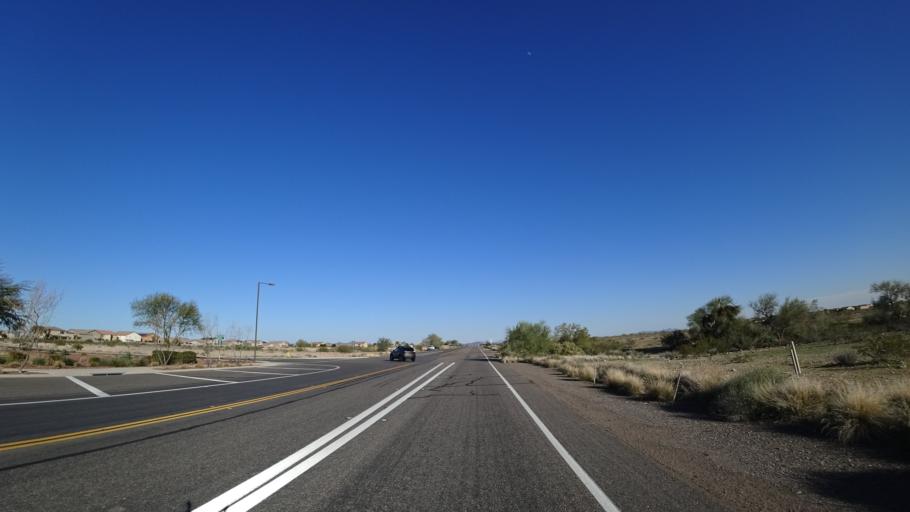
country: US
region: Arizona
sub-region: Maricopa County
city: Sun City West
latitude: 33.6893
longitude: -112.3259
